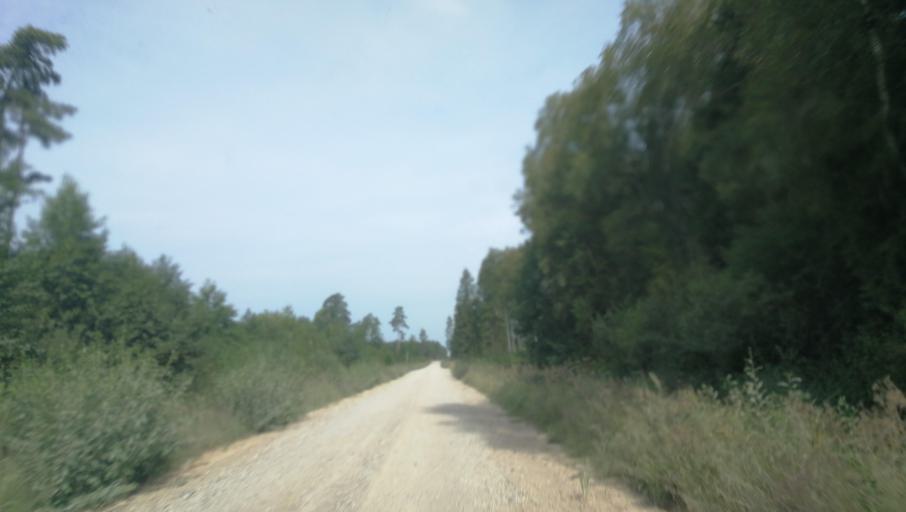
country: LV
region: Durbe
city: Liegi
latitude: 56.7706
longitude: 21.3533
